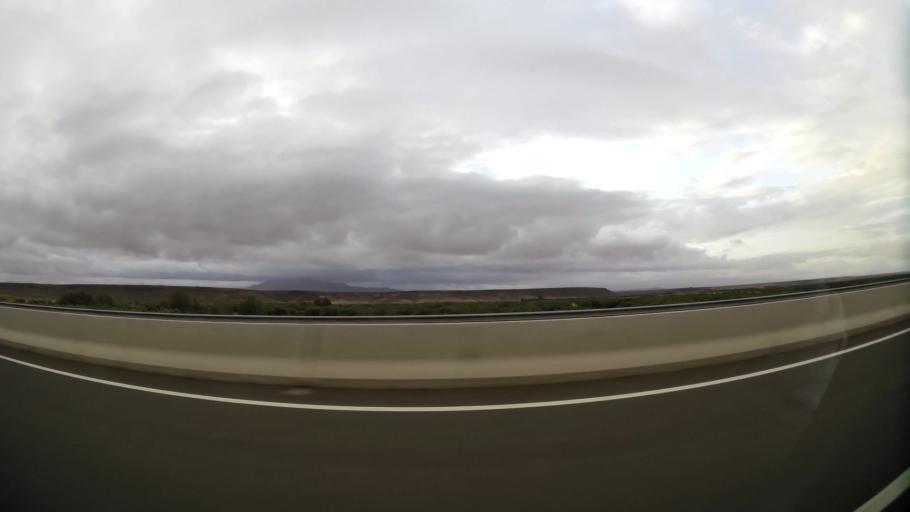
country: MA
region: Taza-Al Hoceima-Taounate
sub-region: Taza
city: Guercif
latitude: 34.3973
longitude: -3.2036
